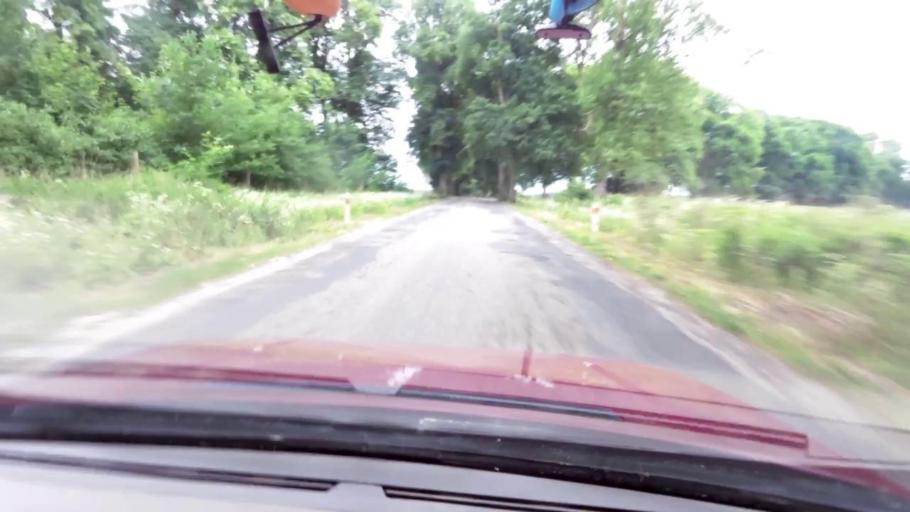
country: PL
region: Pomeranian Voivodeship
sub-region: Powiat slupski
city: Kepice
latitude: 54.2206
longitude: 16.8420
